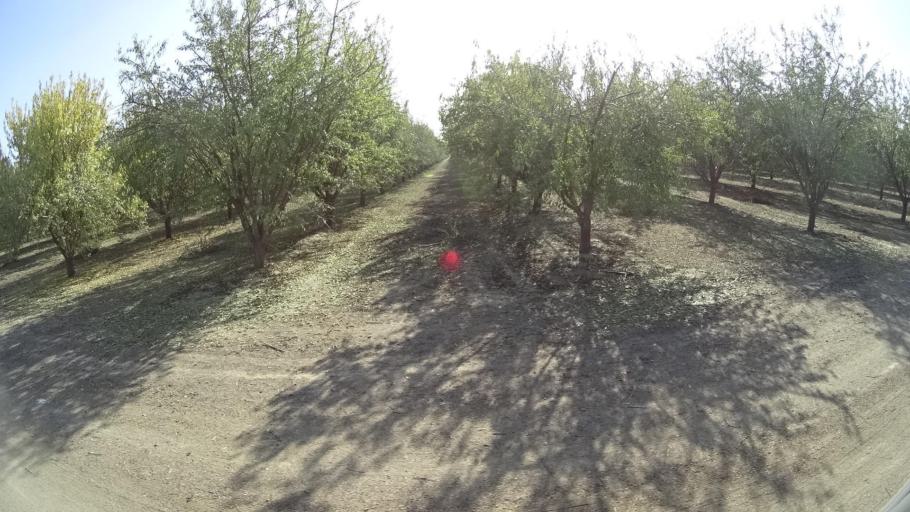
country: US
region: California
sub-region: Kern County
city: McFarland
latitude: 35.6311
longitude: -119.2095
